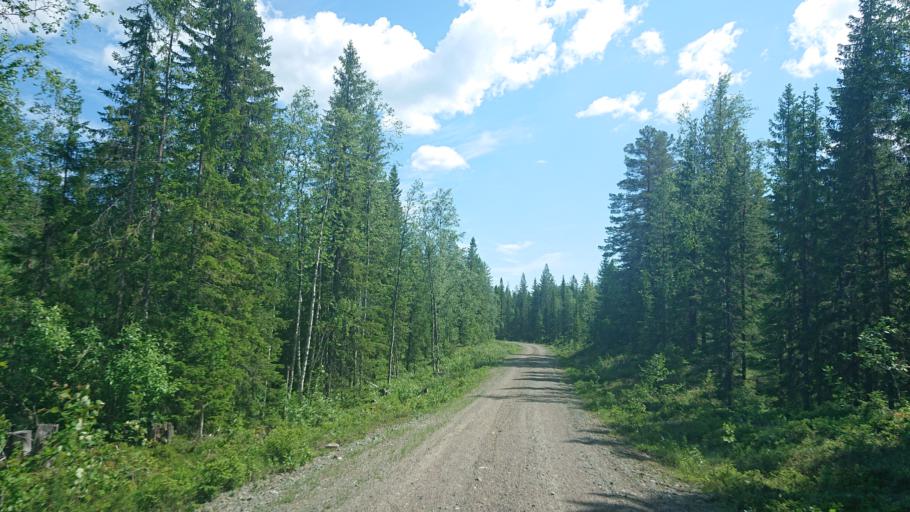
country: SE
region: Vaesternorrland
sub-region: Solleftea Kommun
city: Solleftea
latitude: 62.9339
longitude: 17.0823
